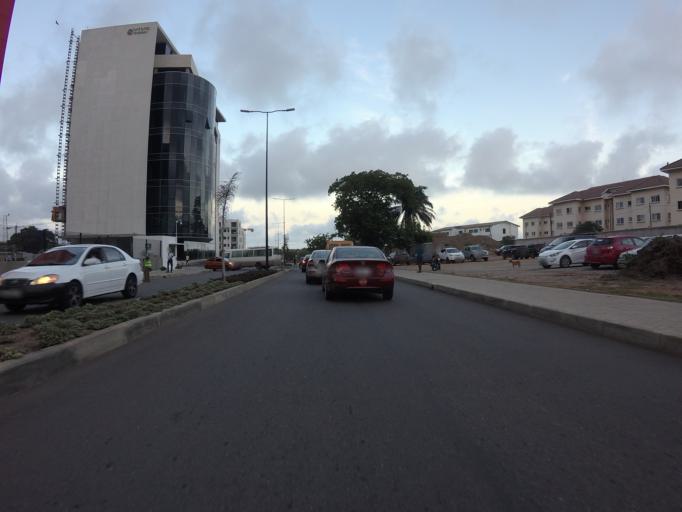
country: GH
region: Greater Accra
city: Accra
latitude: 5.5733
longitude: -0.1827
